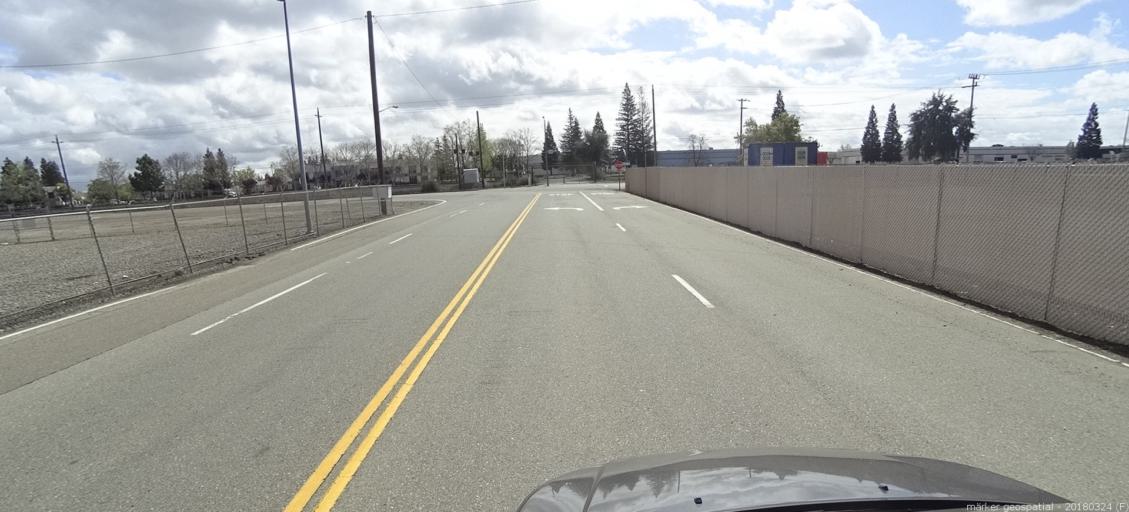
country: US
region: California
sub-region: Sacramento County
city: North Highlands
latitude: 38.6528
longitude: -121.3918
